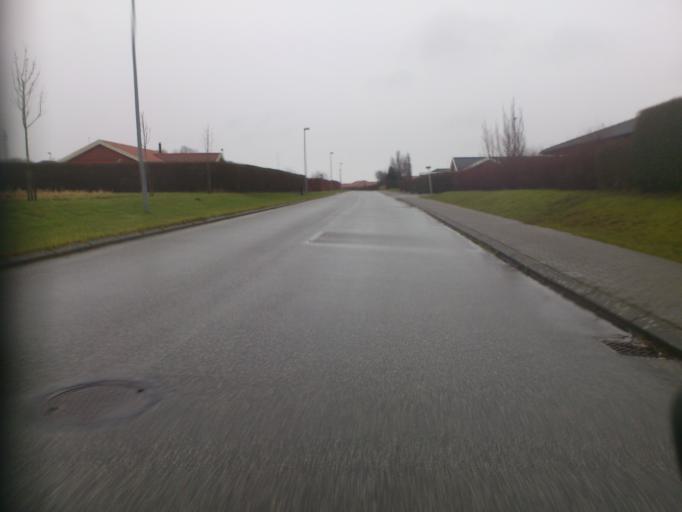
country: DK
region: South Denmark
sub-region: Fredericia Kommune
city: Fredericia
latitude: 55.5758
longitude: 9.7023
